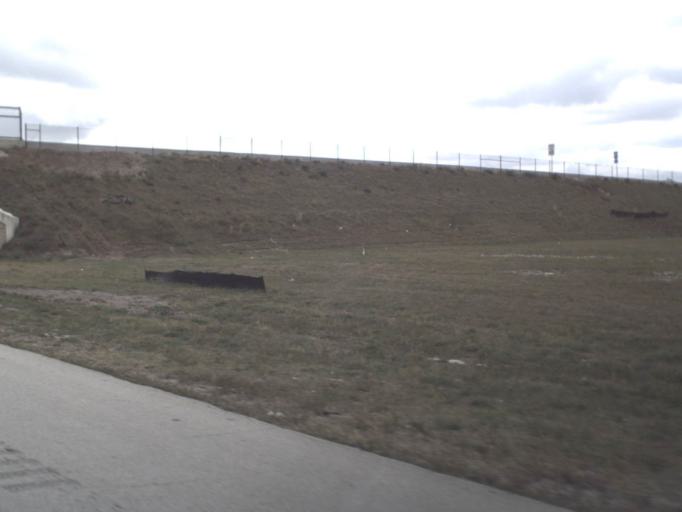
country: US
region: Florida
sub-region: Brevard County
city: South Patrick Shores
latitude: 28.1932
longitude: -80.7079
